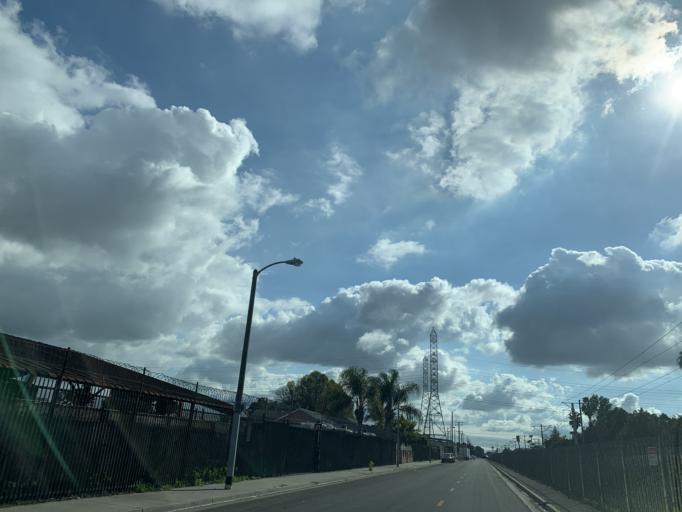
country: US
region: California
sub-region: Los Angeles County
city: Florence-Graham
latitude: 33.9564
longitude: -118.2431
